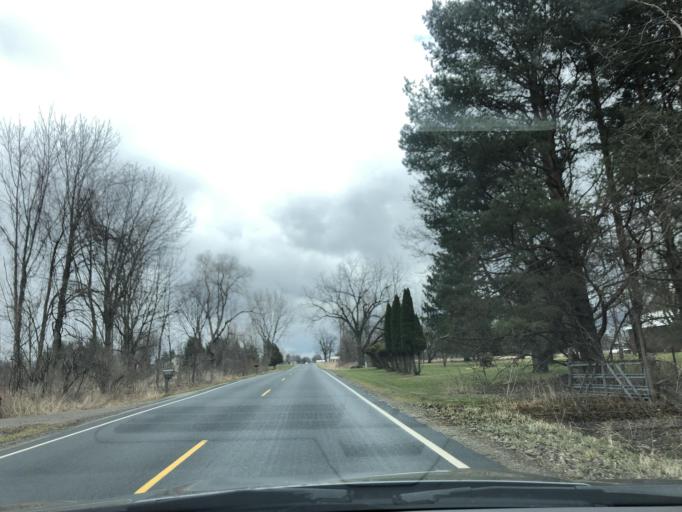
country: US
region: Michigan
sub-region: Clinton County
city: Saint Johns
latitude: 43.0462
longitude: -84.6286
